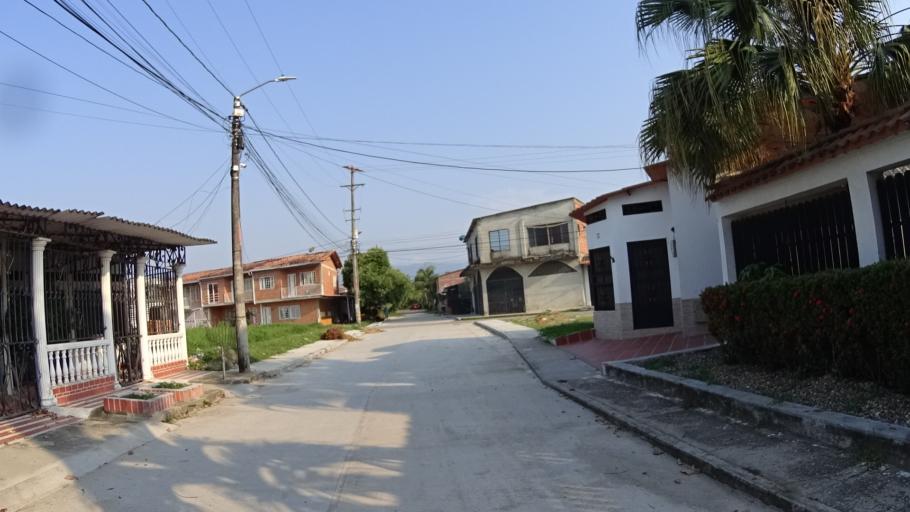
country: CO
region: Cundinamarca
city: Puerto Salgar
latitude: 5.4812
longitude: -74.6735
